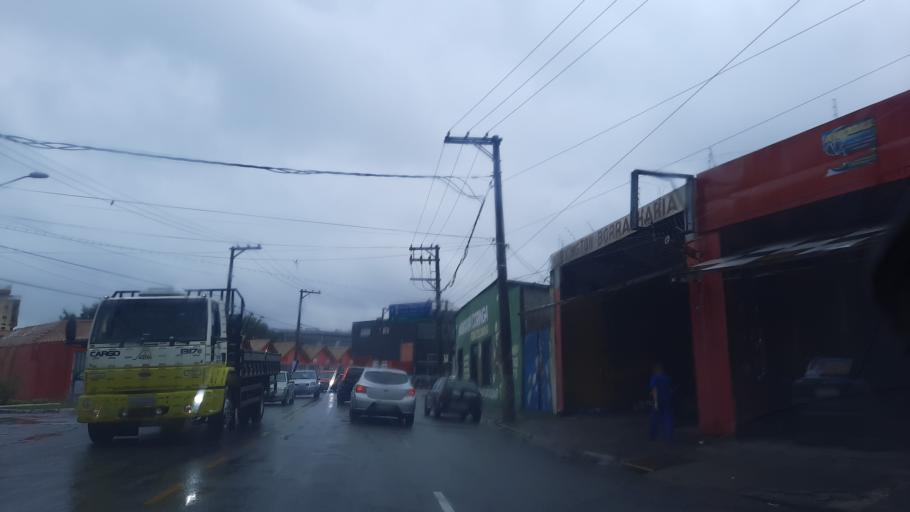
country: BR
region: Sao Paulo
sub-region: Guarulhos
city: Guarulhos
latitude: -23.4607
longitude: -46.5672
